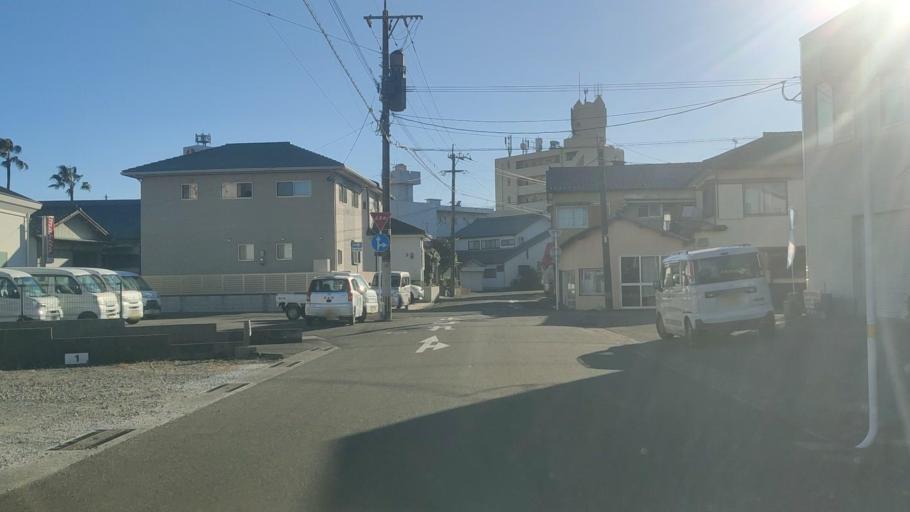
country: JP
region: Miyazaki
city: Miyazaki-shi
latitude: 31.8994
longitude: 131.4241
